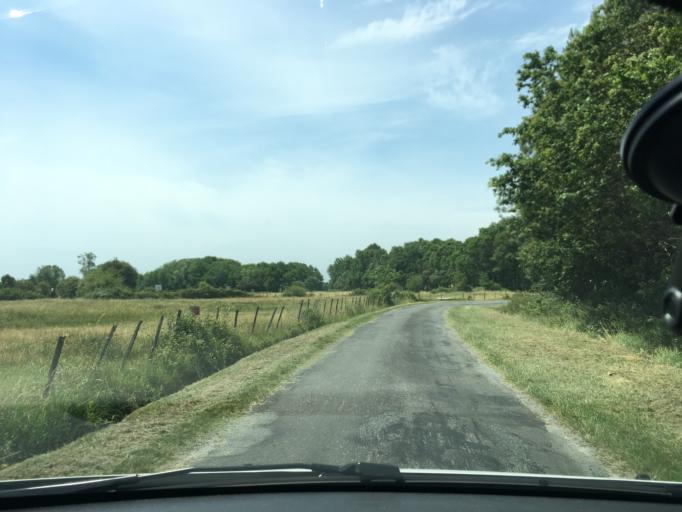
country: FR
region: Aquitaine
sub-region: Departement de la Gironde
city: Lesparre-Medoc
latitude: 45.2770
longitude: -0.9127
